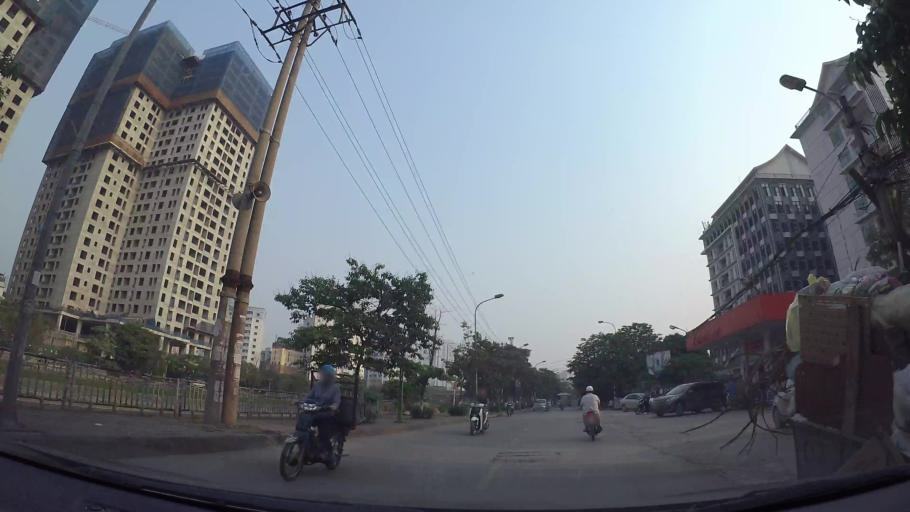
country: VN
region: Ha Noi
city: Thanh Xuan
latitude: 20.9734
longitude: 105.8248
